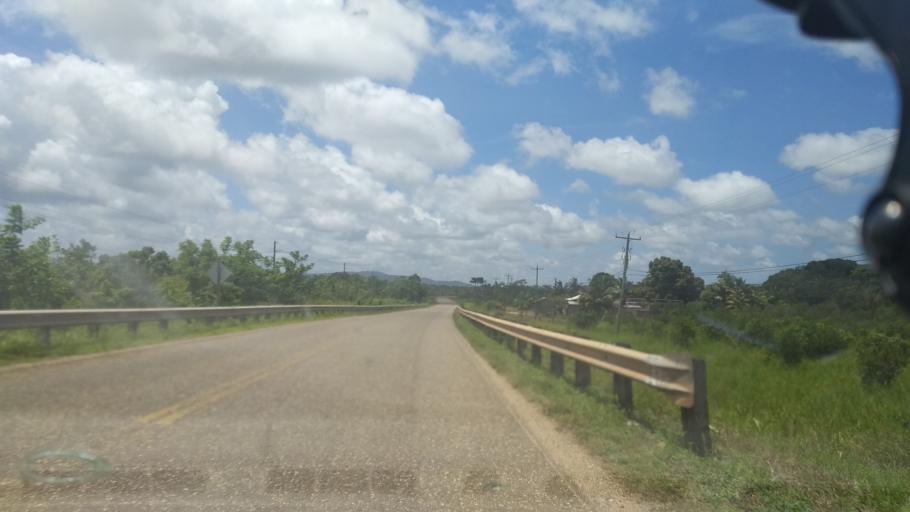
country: BZ
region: Stann Creek
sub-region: Dangriga
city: Dangriga
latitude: 16.8634
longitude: -88.3475
